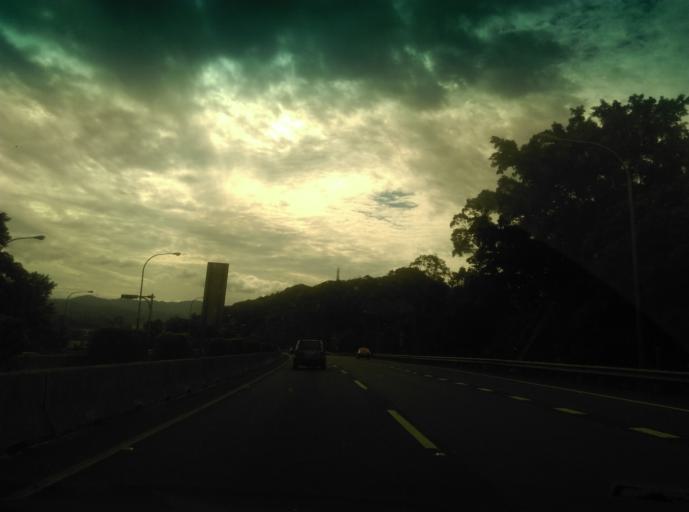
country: TW
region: Taiwan
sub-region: Keelung
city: Keelung
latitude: 25.1173
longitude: 121.7300
